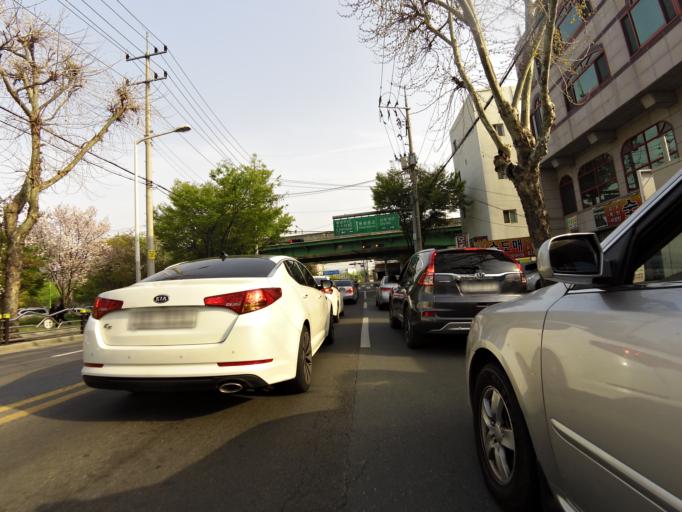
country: KR
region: Daegu
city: Daegu
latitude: 35.8789
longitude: 128.6491
